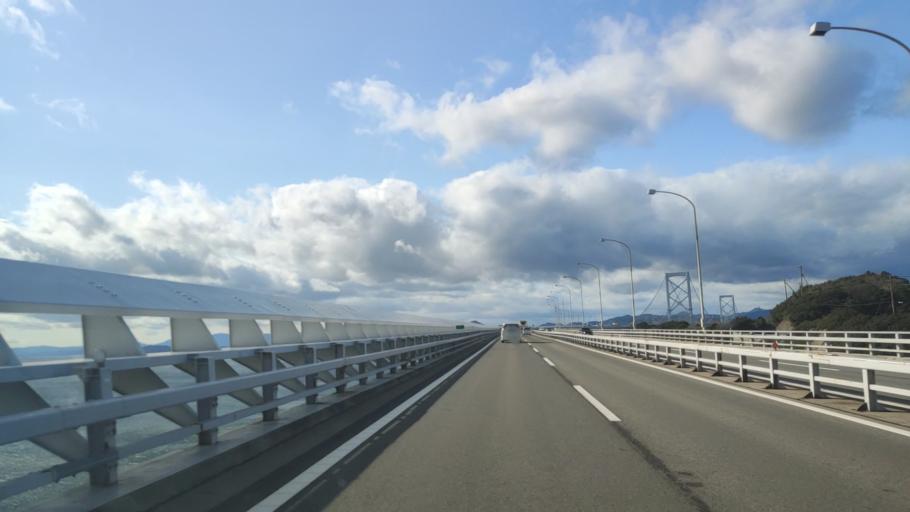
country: JP
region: Hyogo
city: Fukura
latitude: 34.2452
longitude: 134.6671
